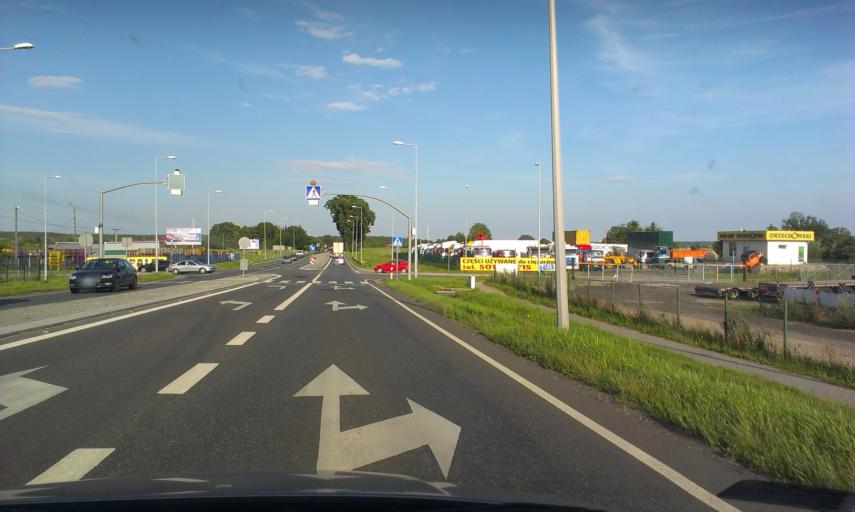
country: PL
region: Kujawsko-Pomorskie
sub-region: Powiat bydgoski
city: Sicienko
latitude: 53.1582
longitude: 17.8481
